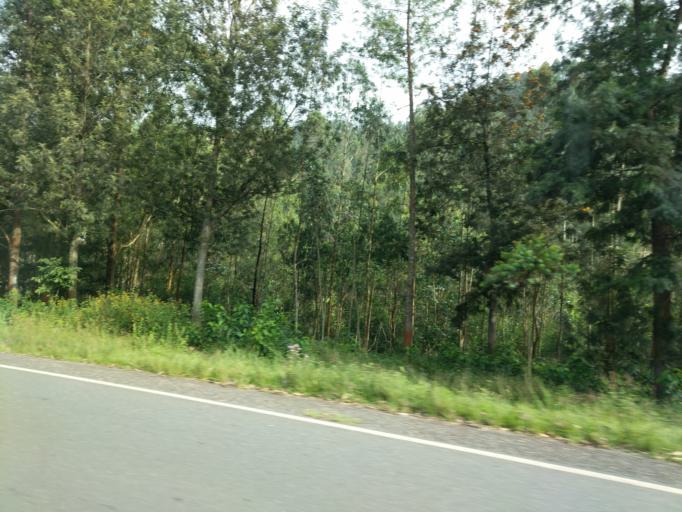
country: RW
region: Northern Province
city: Musanze
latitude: -1.6577
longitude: 29.8141
